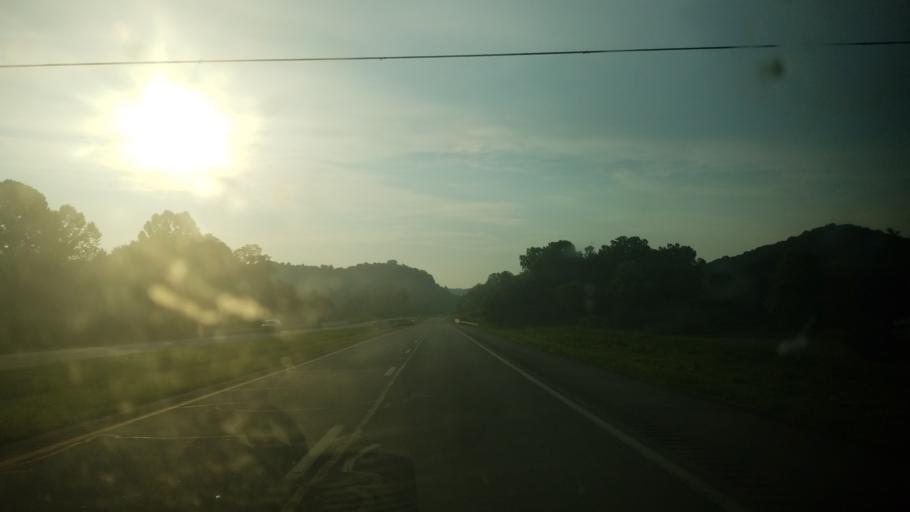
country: US
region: Ohio
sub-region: Pike County
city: Piketon
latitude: 39.0499
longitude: -83.0573
